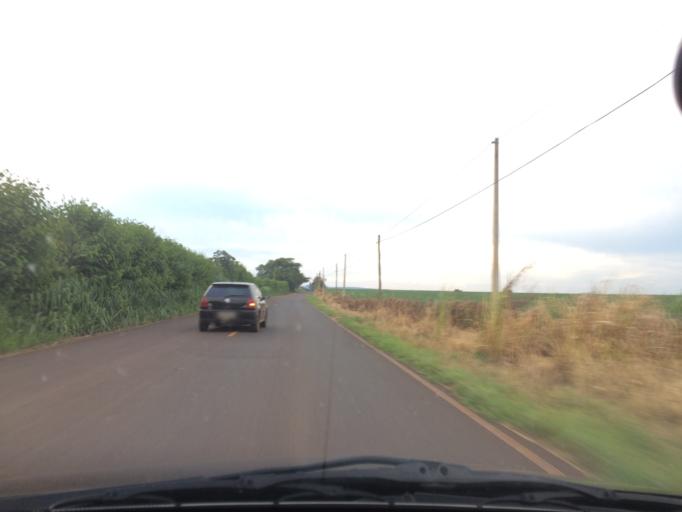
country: BR
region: Sao Paulo
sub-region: Casa Branca
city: Casa Branca
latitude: -21.7579
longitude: -47.1163
